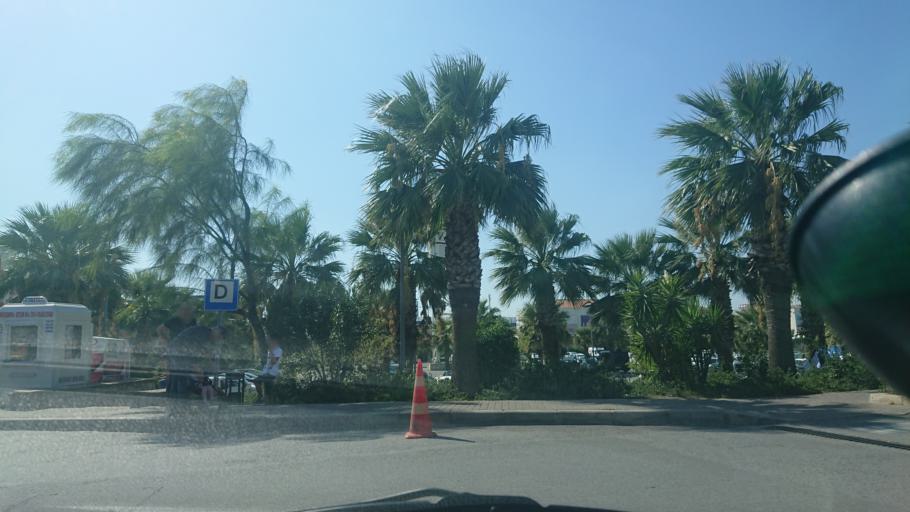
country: TR
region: Izmir
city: Bornova
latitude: 38.4489
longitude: 27.2092
